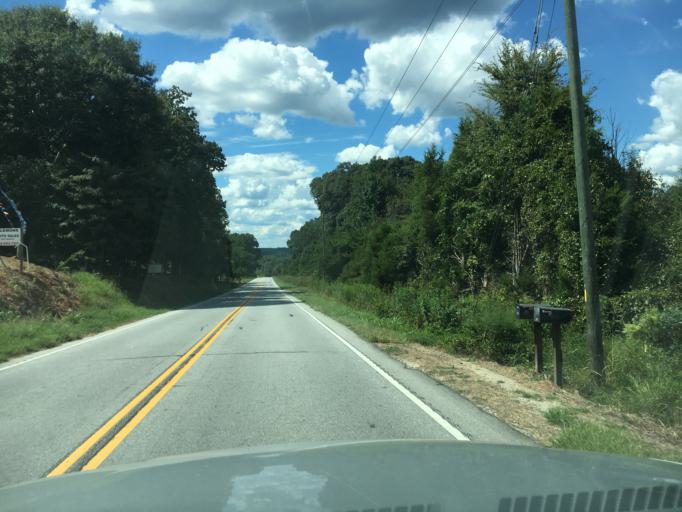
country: US
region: South Carolina
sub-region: Laurens County
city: Laurens
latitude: 34.5228
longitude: -82.1171
